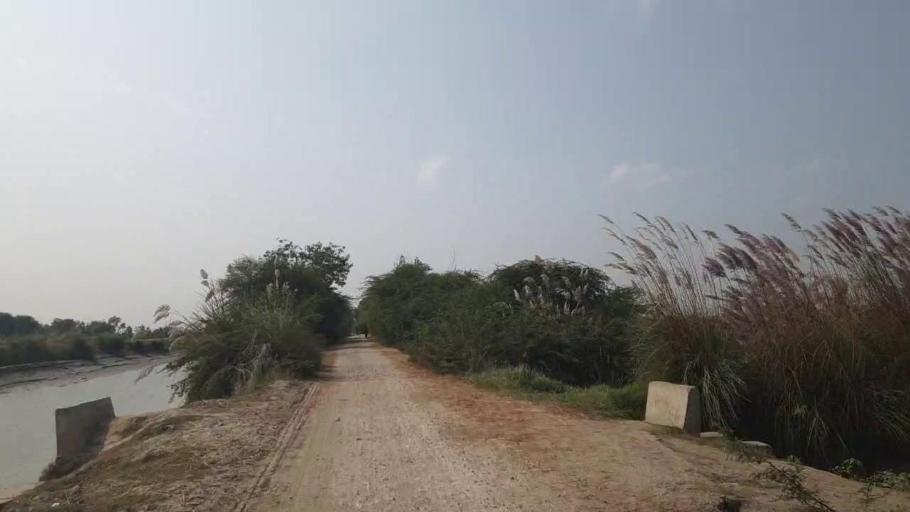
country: PK
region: Sindh
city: Badin
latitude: 24.7616
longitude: 68.7593
